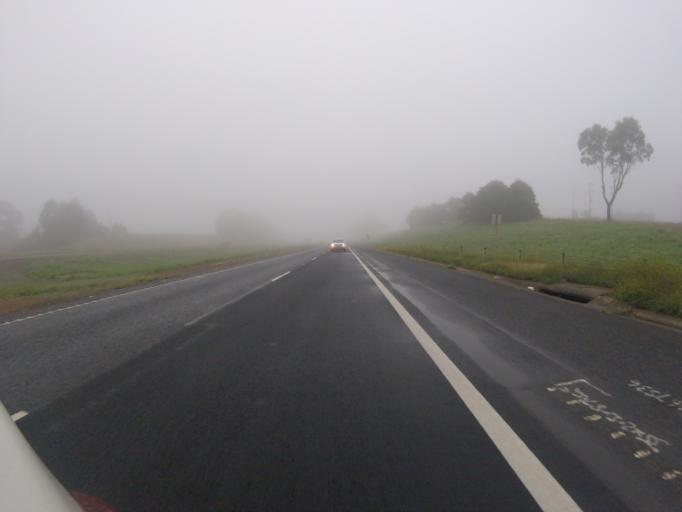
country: AU
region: Victoria
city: Brown Hill
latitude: -37.5517
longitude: 144.0706
